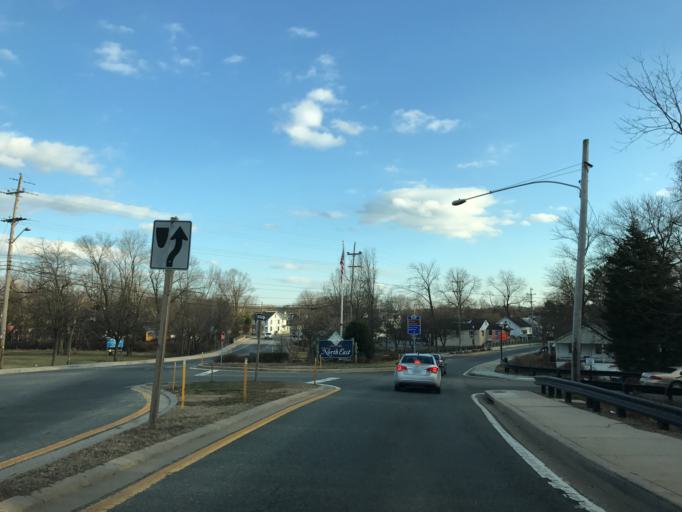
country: US
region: Maryland
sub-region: Cecil County
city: North East
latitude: 39.6033
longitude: -75.9439
